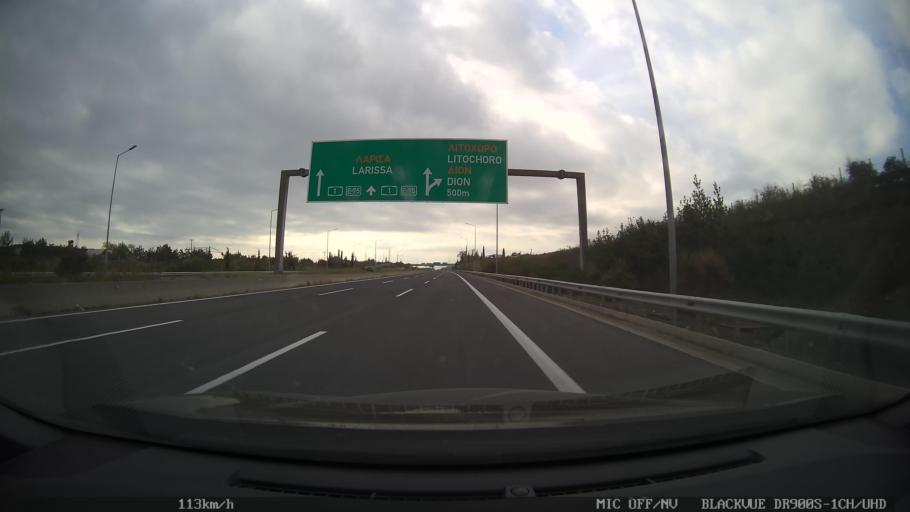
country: GR
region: Central Macedonia
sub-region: Nomos Pierias
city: Litochoro
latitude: 40.1375
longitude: 22.5442
